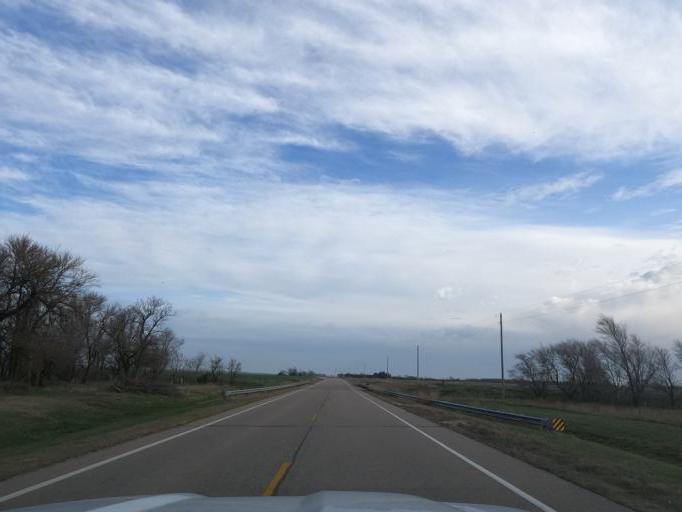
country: US
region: Kansas
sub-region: Reno County
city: Nickerson
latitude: 38.0523
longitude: -98.1791
